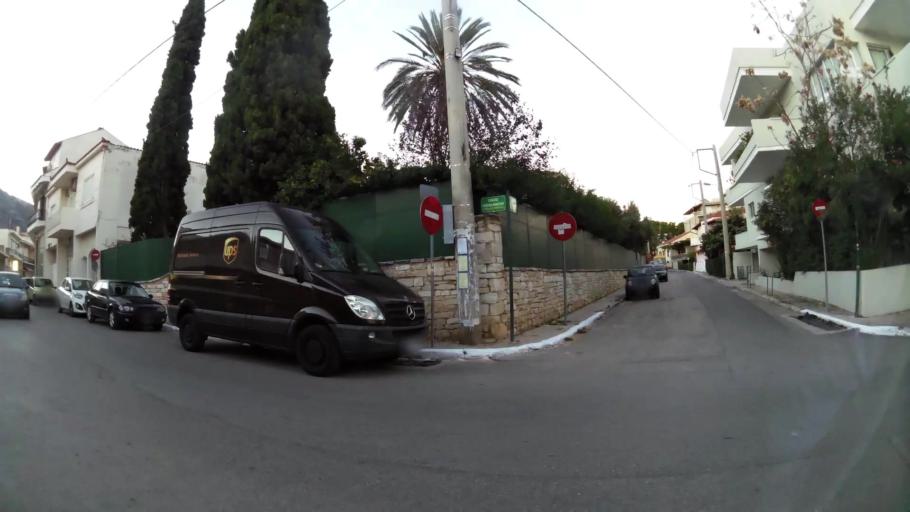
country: GR
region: Attica
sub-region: Nomarchia Anatolikis Attikis
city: Paiania
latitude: 37.9520
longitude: 23.8533
